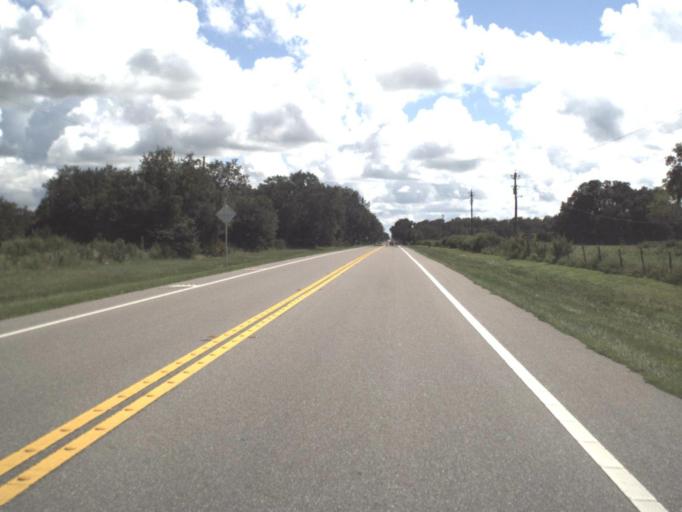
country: US
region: Florida
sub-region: Sarasota County
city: Lake Sarasota
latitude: 27.3834
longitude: -82.2419
